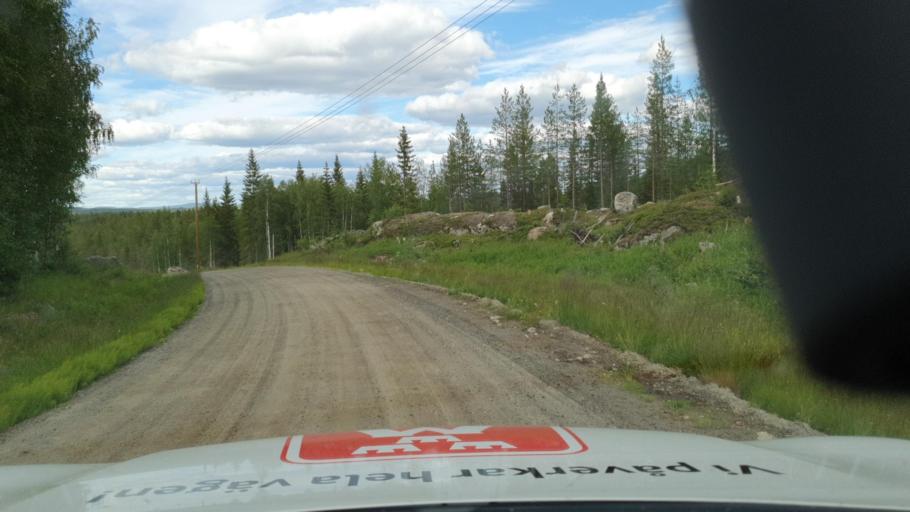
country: SE
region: Vaesterbotten
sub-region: Lycksele Kommun
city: Soderfors
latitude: 64.2618
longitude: 18.0952
